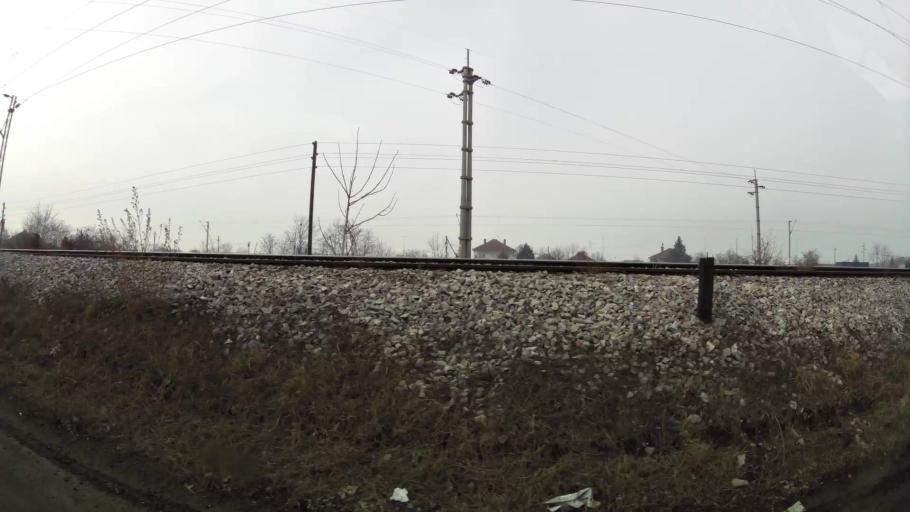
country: MK
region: Ilinden
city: Ilinden
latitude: 41.9974
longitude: 21.5618
